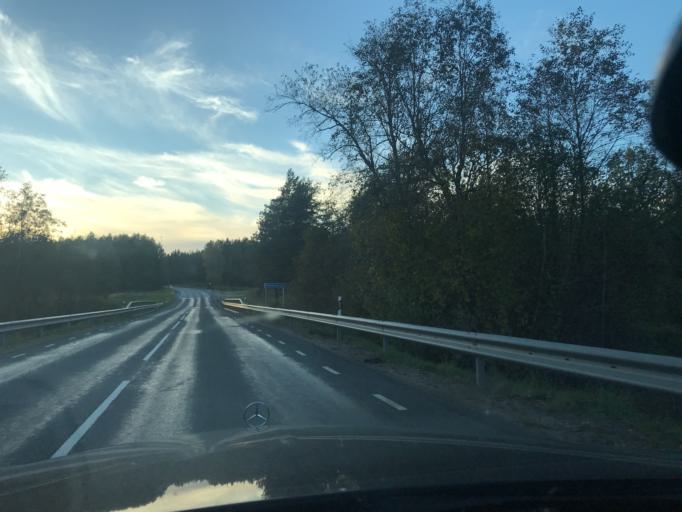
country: EE
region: Vorumaa
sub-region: Antsla vald
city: Vana-Antsla
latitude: 57.8828
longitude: 26.7397
